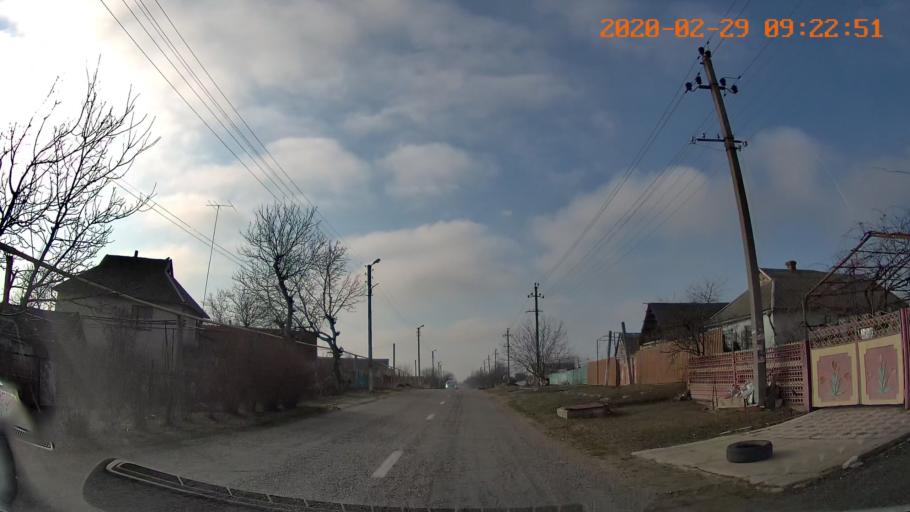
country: MD
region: Telenesti
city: Pervomaisc
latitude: 46.7317
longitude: 29.9630
